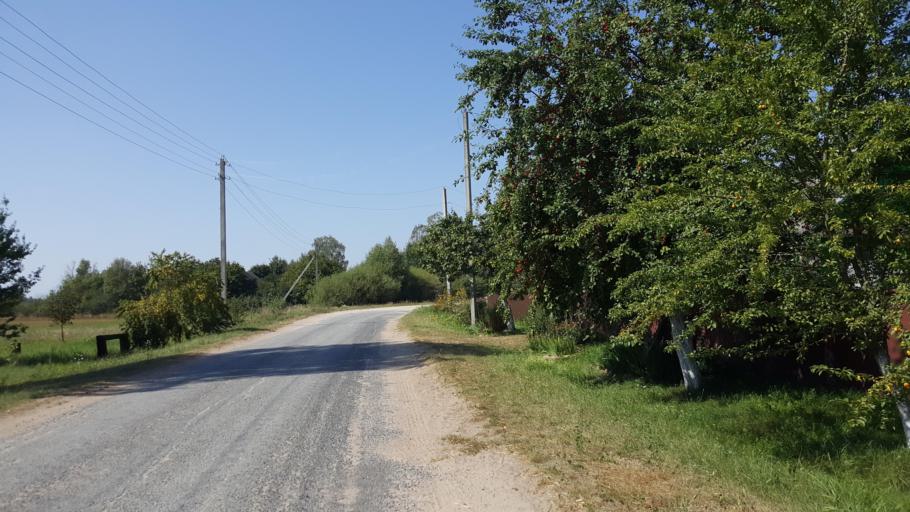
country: BY
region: Brest
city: Vysokaye
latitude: 52.4491
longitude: 23.4464
